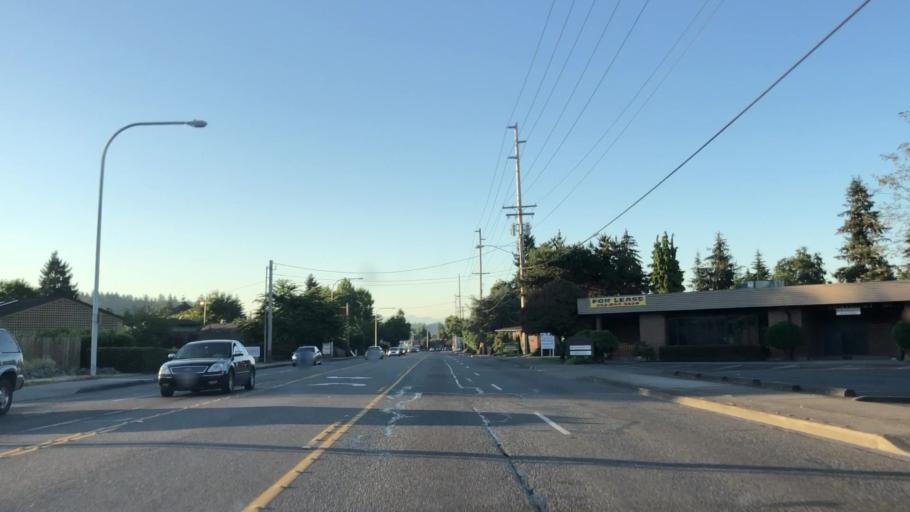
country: US
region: Washington
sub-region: King County
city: Auburn
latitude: 47.3182
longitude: -122.2180
